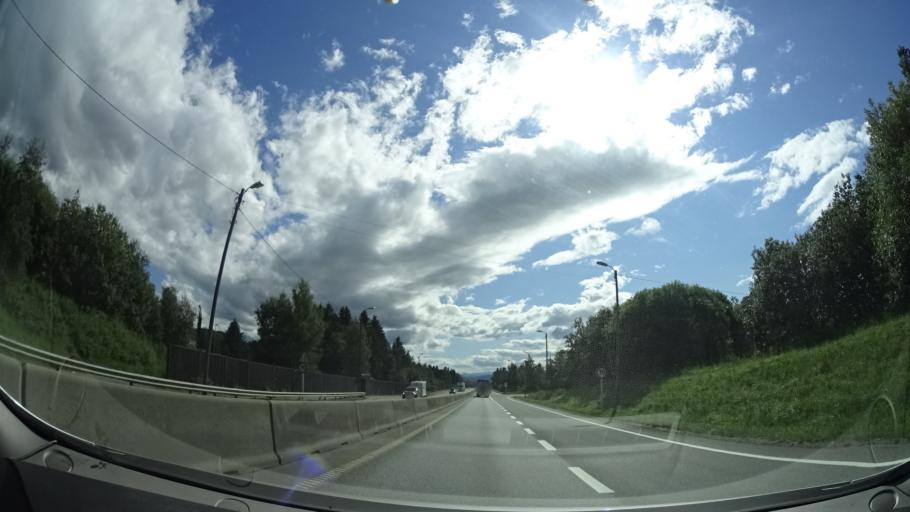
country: NO
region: Sor-Trondelag
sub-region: Trondheim
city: Trondheim
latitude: 63.3398
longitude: 10.3632
